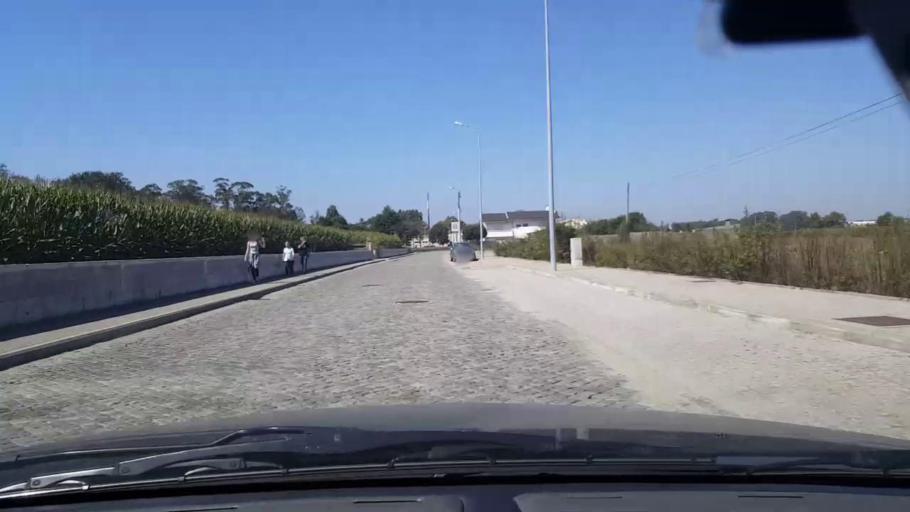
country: PT
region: Porto
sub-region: Vila do Conde
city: Arvore
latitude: 41.3062
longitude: -8.7169
